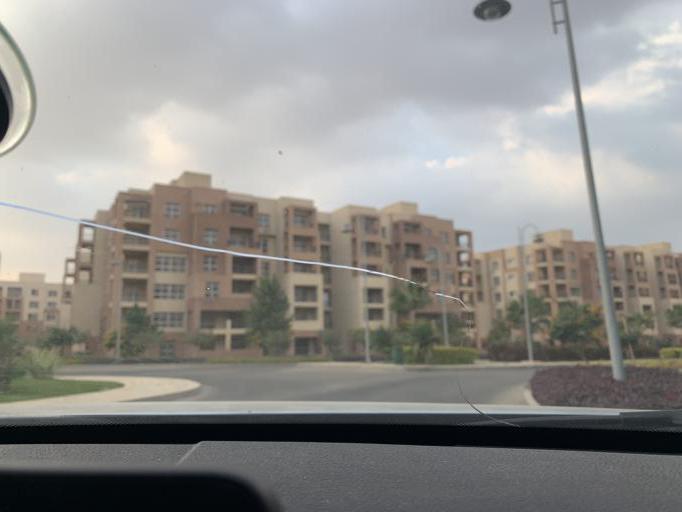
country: EG
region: Muhafazat al Qalyubiyah
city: Al Khankah
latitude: 30.1032
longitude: 31.6516
